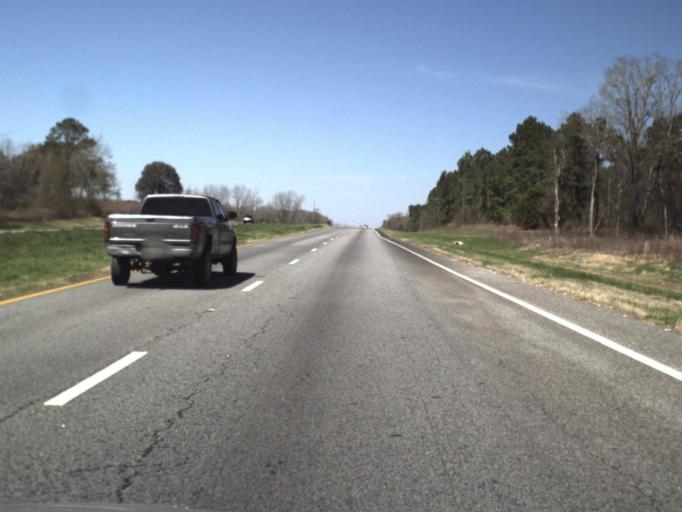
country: US
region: Florida
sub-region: Jackson County
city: Marianna
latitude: 30.8459
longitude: -85.3469
